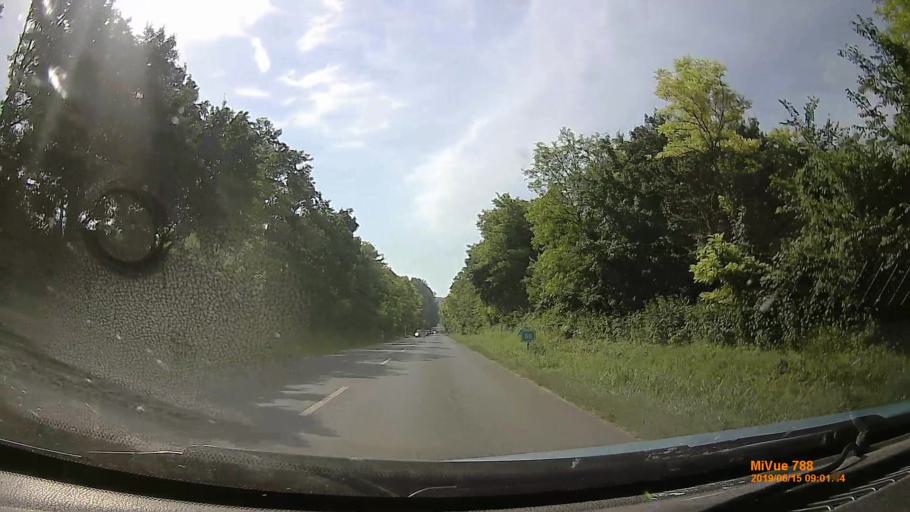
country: HU
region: Tolna
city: Iregszemcse
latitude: 46.7631
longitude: 18.1538
